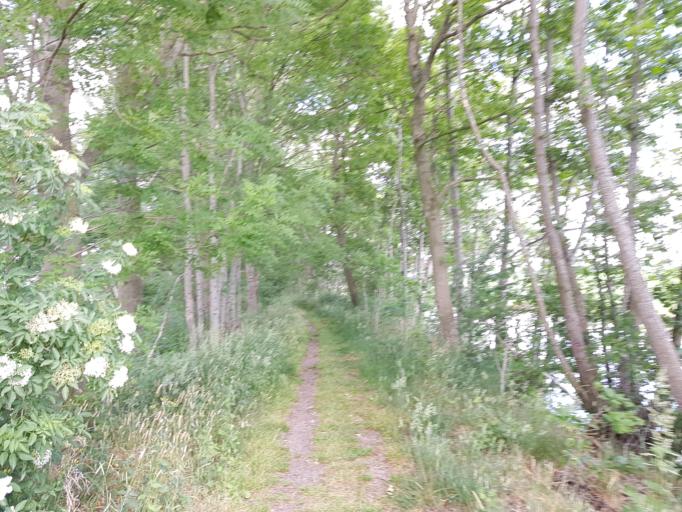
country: NL
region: Utrecht
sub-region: Gemeente Montfoort
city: Montfoort
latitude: 52.0211
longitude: 4.9831
